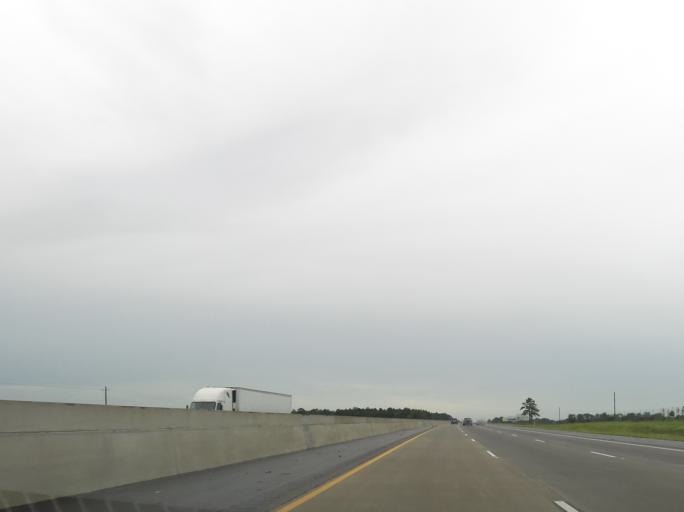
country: US
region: Georgia
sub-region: Tift County
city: Omega
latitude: 31.3134
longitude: -83.4788
